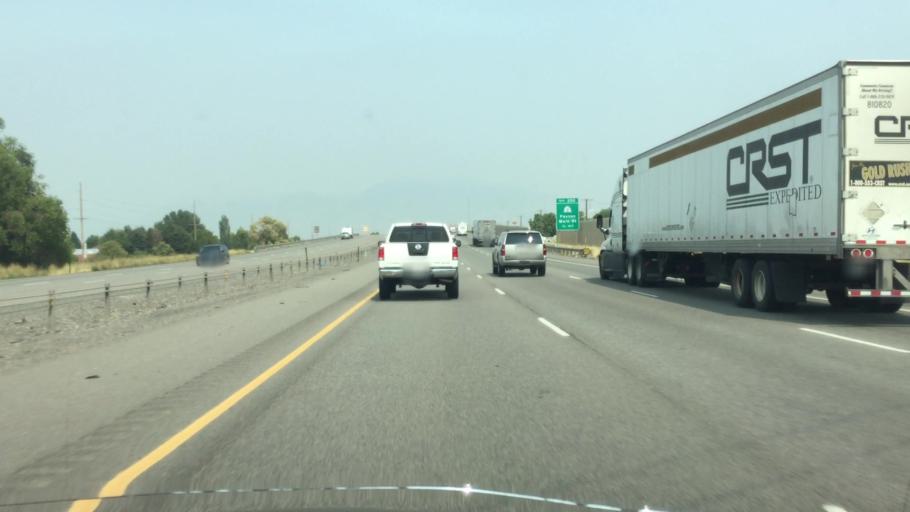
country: US
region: Utah
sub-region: Utah County
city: Payson
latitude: 40.0459
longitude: -111.7425
